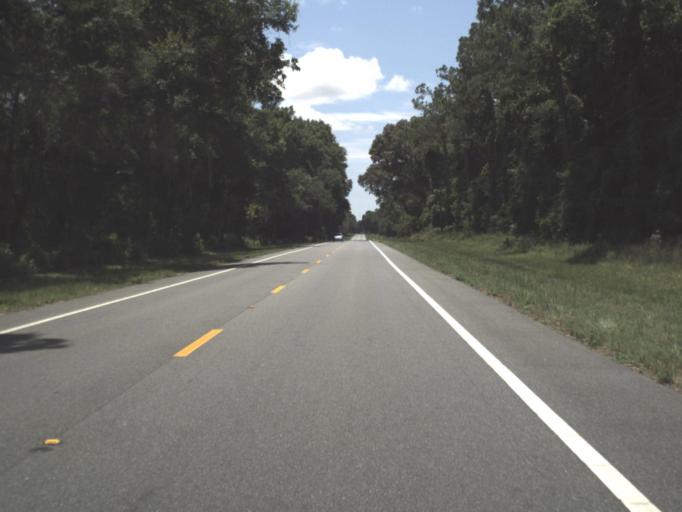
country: US
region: Florida
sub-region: Dixie County
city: Cross City
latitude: 29.8525
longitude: -82.9637
